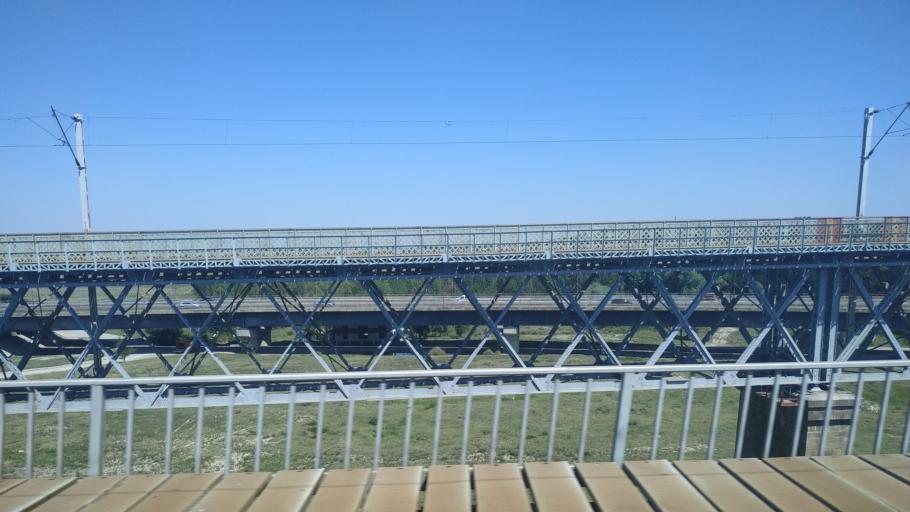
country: RO
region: Constanta
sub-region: Oras Cernavoda
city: Cernavoda
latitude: 44.3438
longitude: 28.0021
